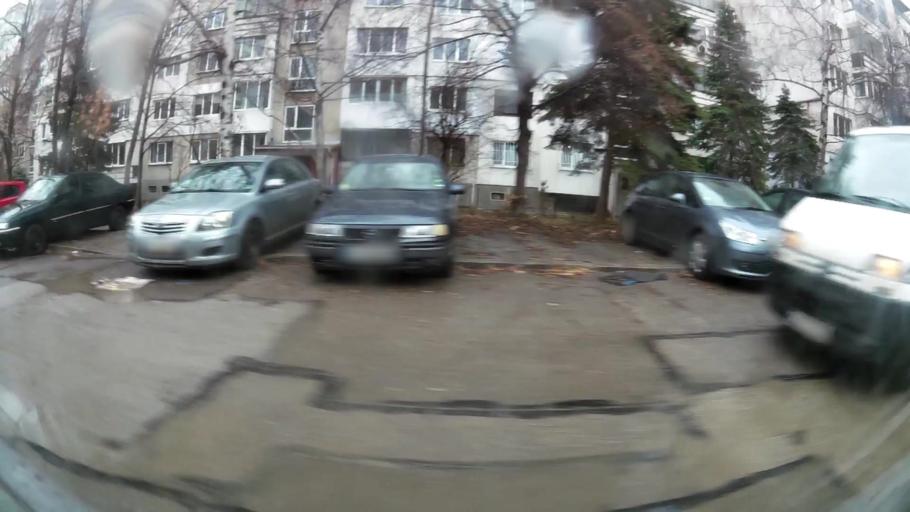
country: BG
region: Sofia-Capital
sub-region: Stolichna Obshtina
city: Sofia
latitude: 42.6445
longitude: 23.3735
